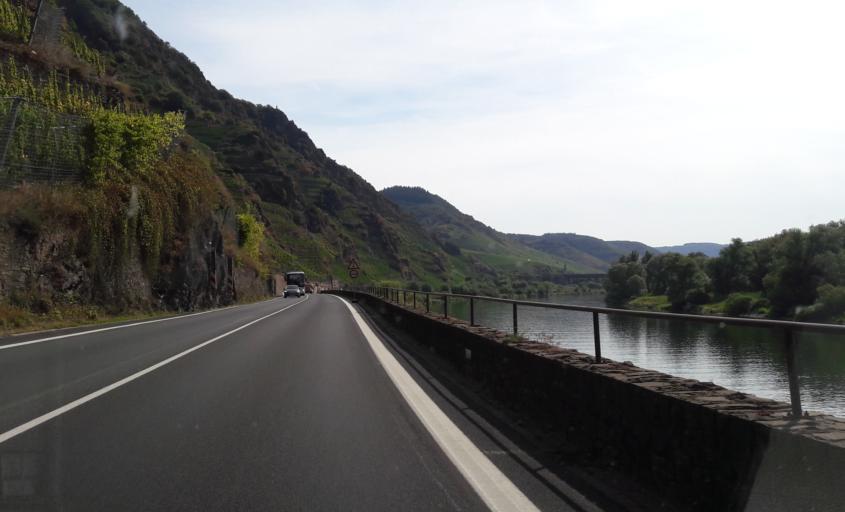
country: DE
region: Rheinland-Pfalz
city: Bremm
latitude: 50.1062
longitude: 7.1232
